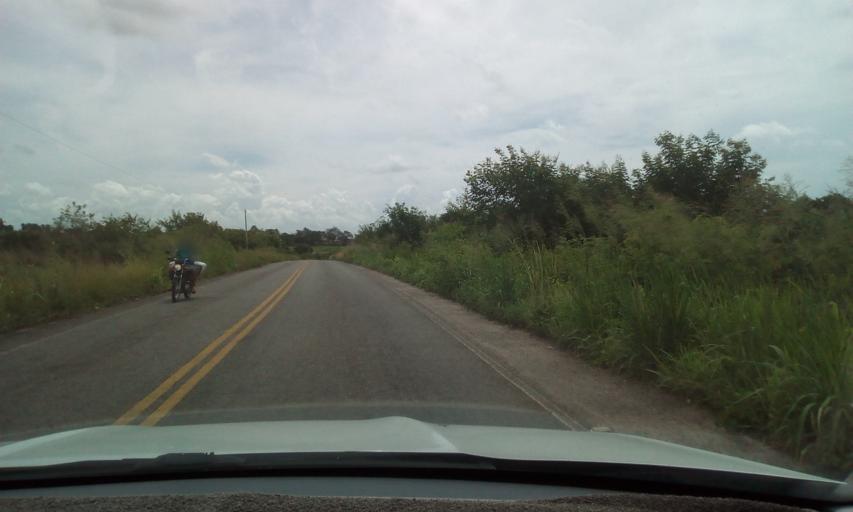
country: BR
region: Paraiba
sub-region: Mari
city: Mari
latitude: -7.1206
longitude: -35.3449
